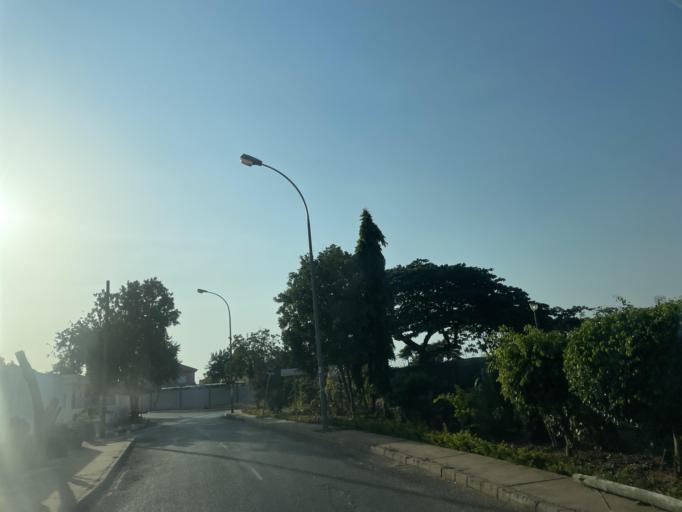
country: AO
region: Luanda
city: Luanda
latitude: -8.9124
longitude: 13.1812
